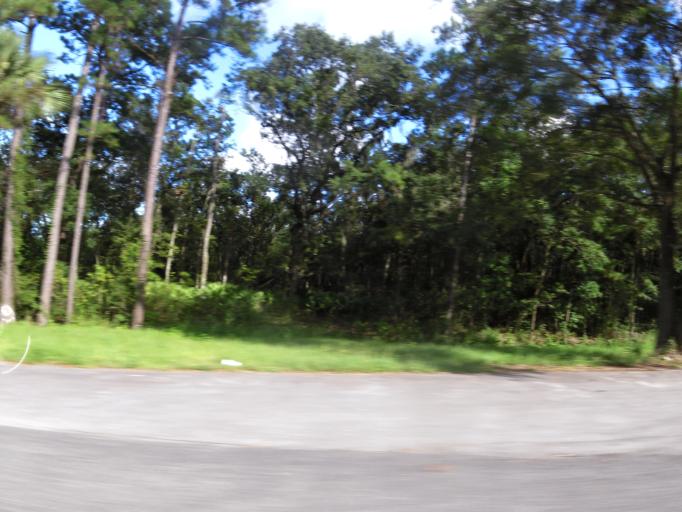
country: US
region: Georgia
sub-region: Glynn County
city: Dock Junction
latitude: 31.1343
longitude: -81.5978
